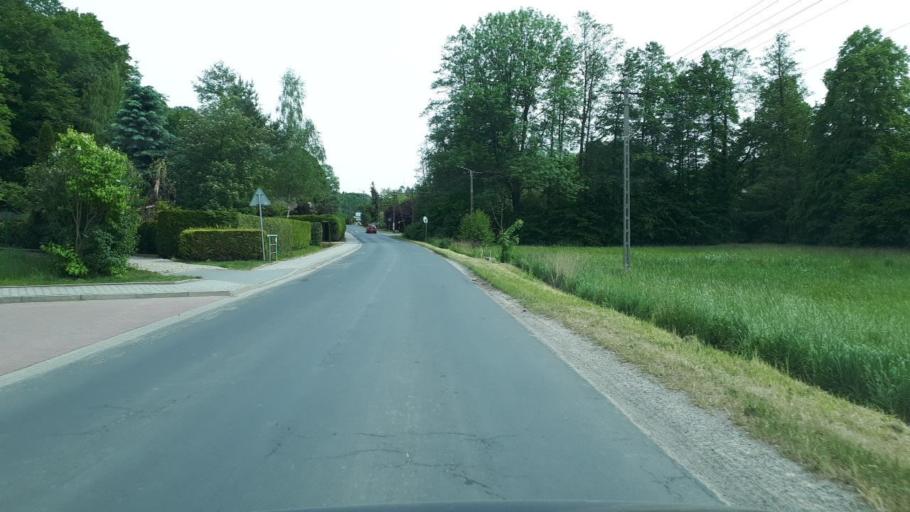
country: PL
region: Silesian Voivodeship
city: Janowice
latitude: 49.9067
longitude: 19.1152
